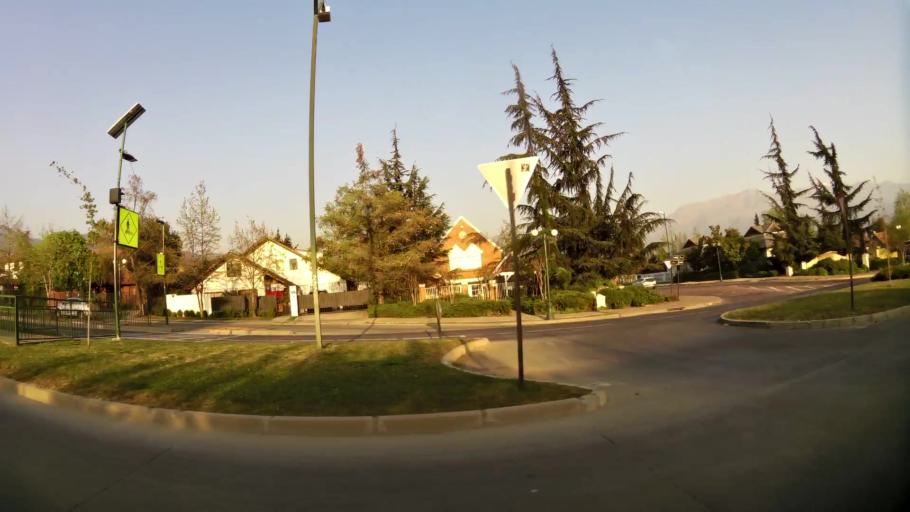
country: CL
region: Santiago Metropolitan
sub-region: Provincia de Chacabuco
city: Chicureo Abajo
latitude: -33.3302
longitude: -70.5198
